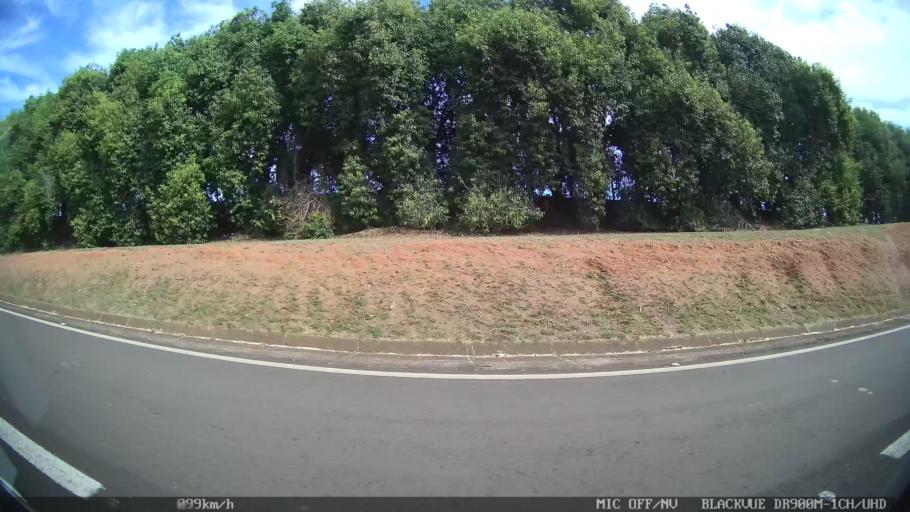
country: BR
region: Sao Paulo
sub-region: Matao
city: Matao
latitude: -21.6349
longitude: -48.4002
